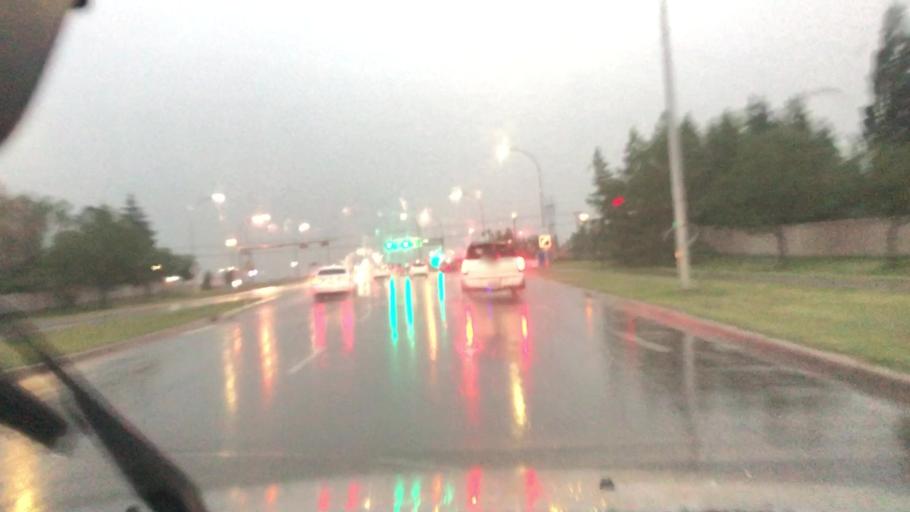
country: CA
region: Alberta
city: Edmonton
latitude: 53.4406
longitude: -113.5184
